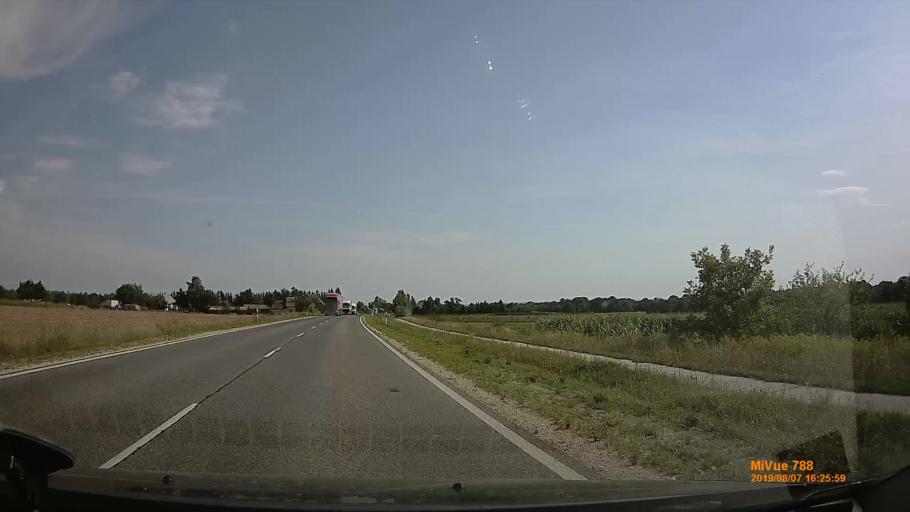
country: HU
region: Zala
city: Lenti
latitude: 46.7150
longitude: 16.5512
